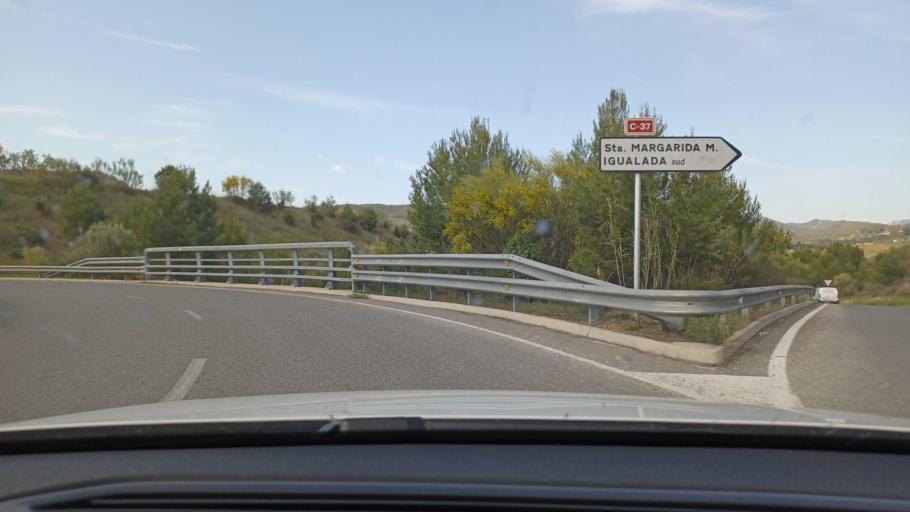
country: ES
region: Catalonia
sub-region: Provincia de Barcelona
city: Vilanova del Cami
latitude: 41.5730
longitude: 1.6535
